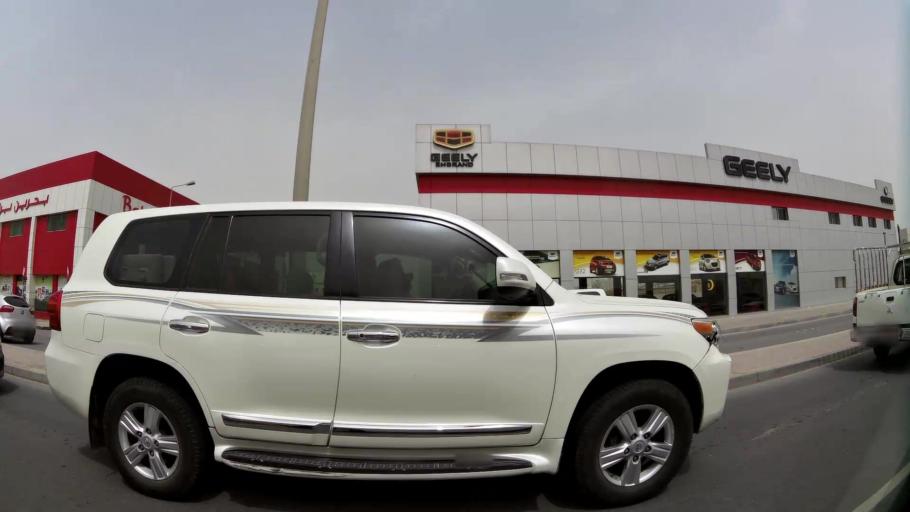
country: BH
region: Northern
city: Madinat `Isa
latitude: 26.1868
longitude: 50.5382
